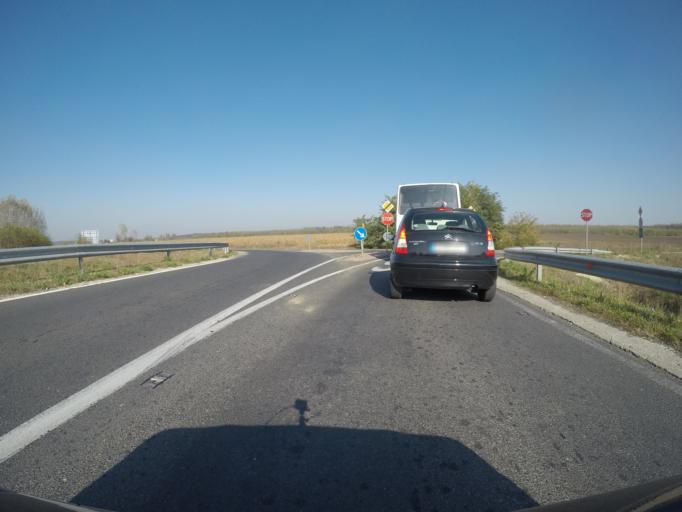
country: HU
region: Tolna
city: Szedres
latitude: 46.4967
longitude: 18.6731
